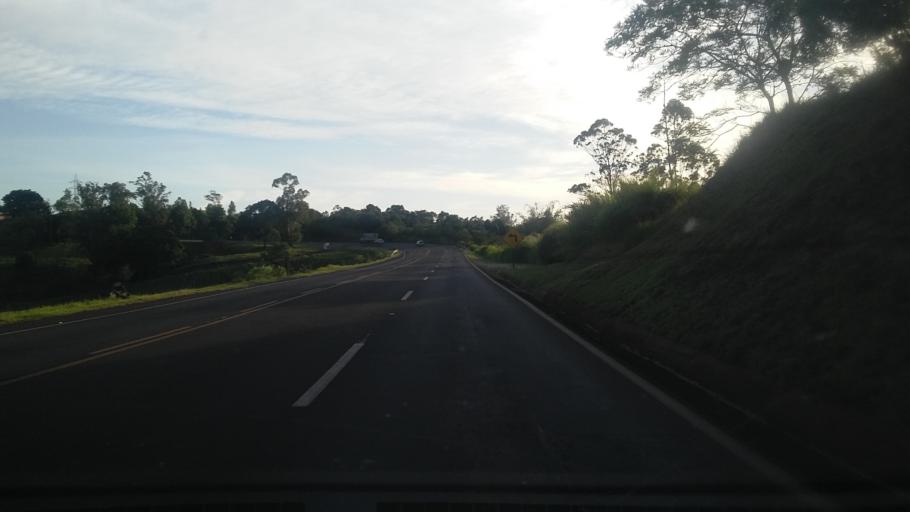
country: BR
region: Parana
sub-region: Assai
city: Assai
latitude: -23.2068
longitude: -50.6575
